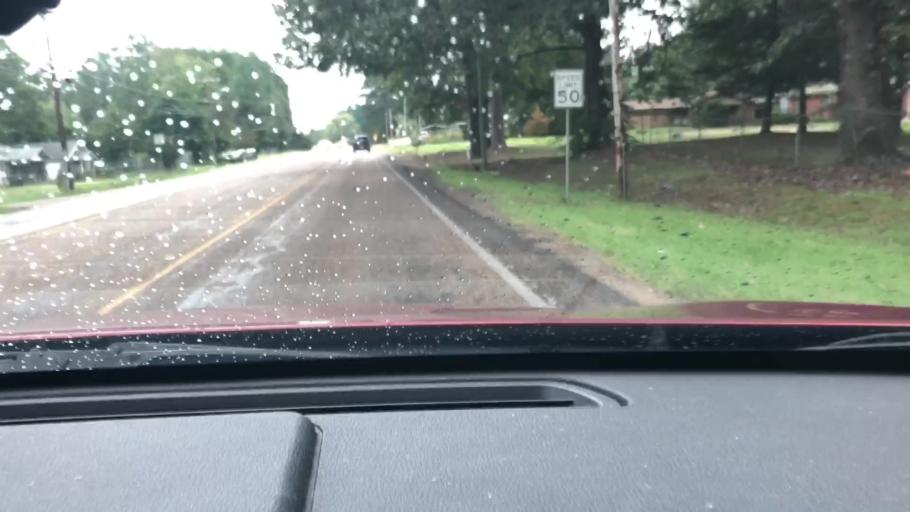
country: US
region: Texas
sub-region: Bowie County
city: Nash
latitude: 33.4427
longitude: -94.1161
